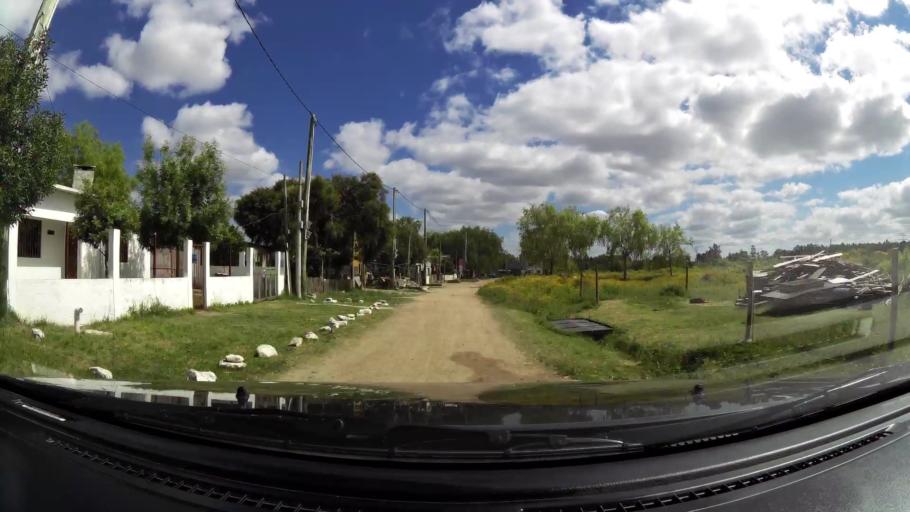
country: UY
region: Canelones
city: Paso de Carrasco
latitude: -34.8588
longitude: -56.1128
